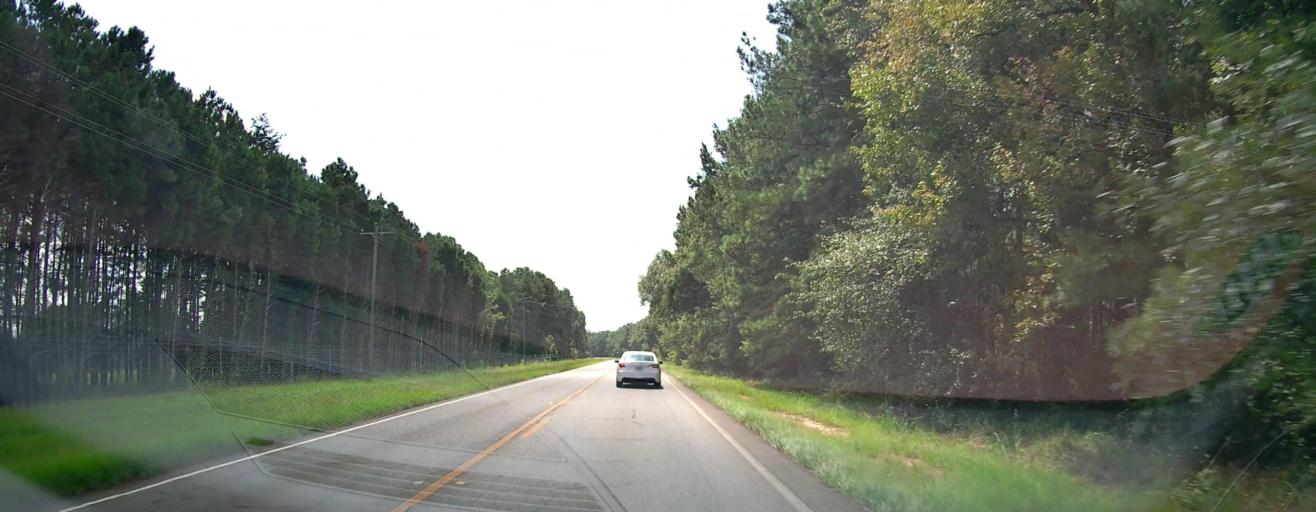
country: US
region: Georgia
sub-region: Houston County
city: Robins Air Force Base
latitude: 32.6267
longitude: -83.4966
